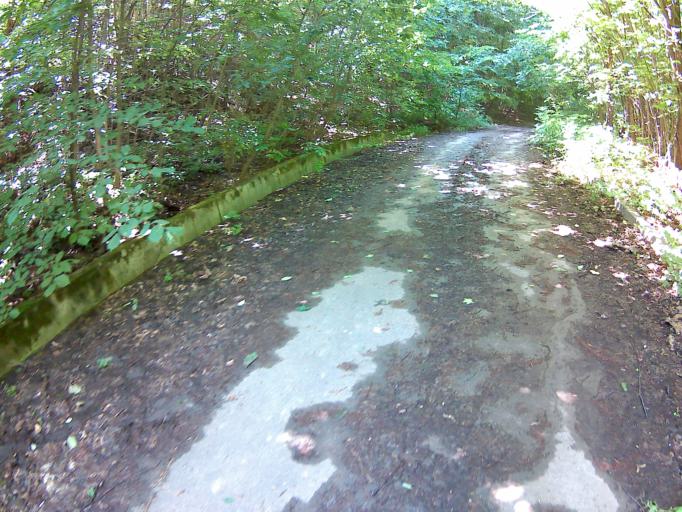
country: RU
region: Nizjnij Novgorod
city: Nizhniy Novgorod
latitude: 56.2328
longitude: 43.9297
